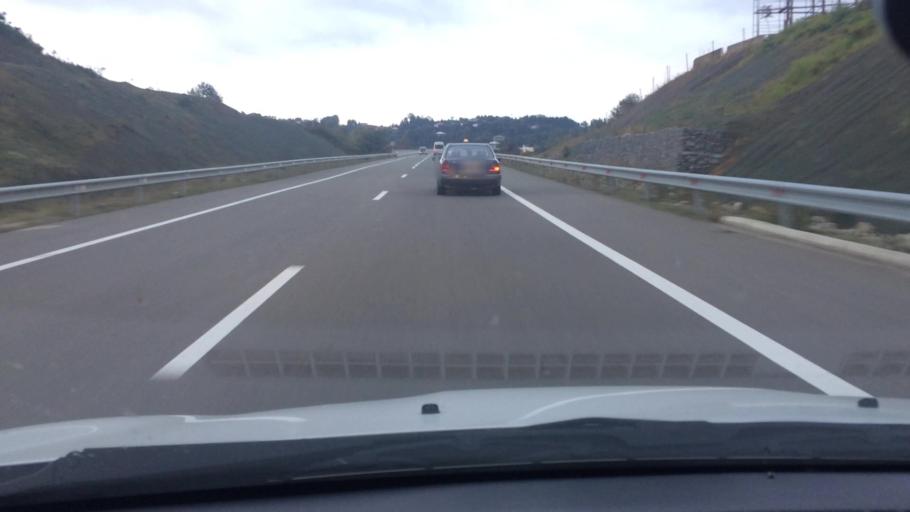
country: GE
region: Ajaria
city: Makhinjauri
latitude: 41.7288
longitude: 41.7516
